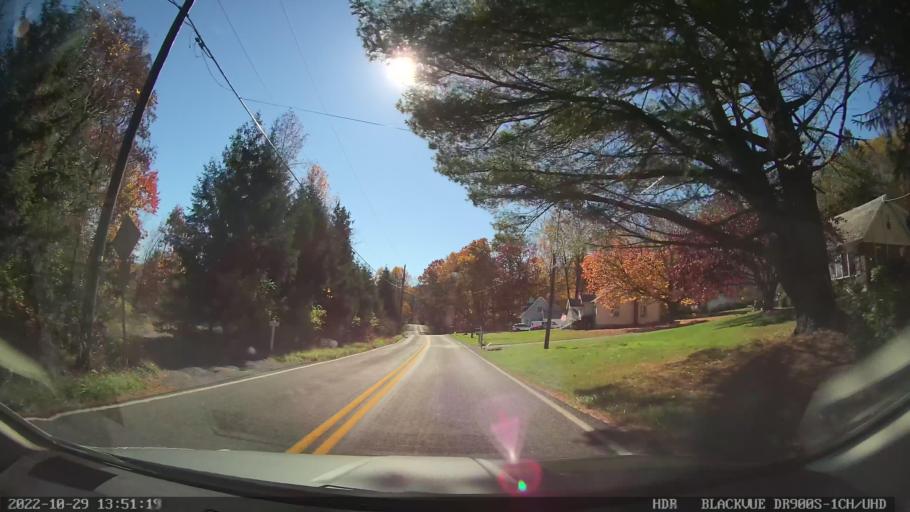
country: US
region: Pennsylvania
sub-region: Lehigh County
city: Emmaus
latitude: 40.5285
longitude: -75.4660
